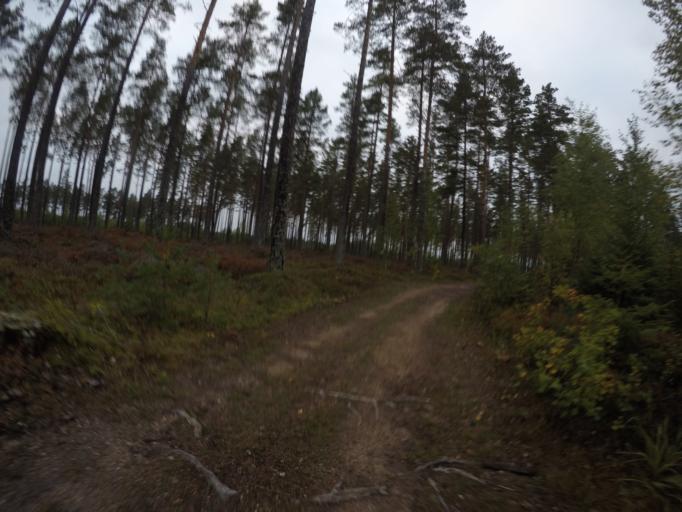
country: SE
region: Vaestmanland
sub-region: Kungsors Kommun
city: Kungsoer
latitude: 59.3727
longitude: 16.1148
